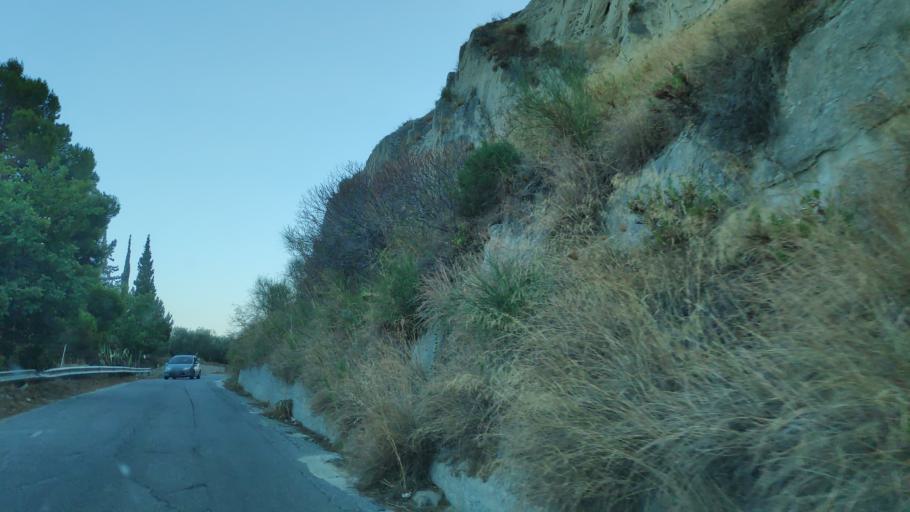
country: IT
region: Calabria
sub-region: Provincia di Reggio Calabria
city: Bova Marina
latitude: 37.9484
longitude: 15.9203
